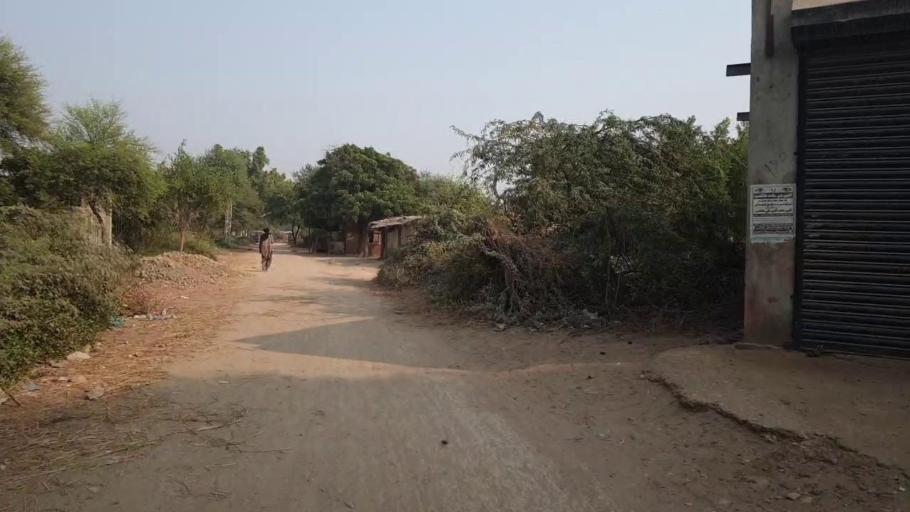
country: PK
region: Sindh
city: Tando Muhammad Khan
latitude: 25.1434
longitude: 68.6124
